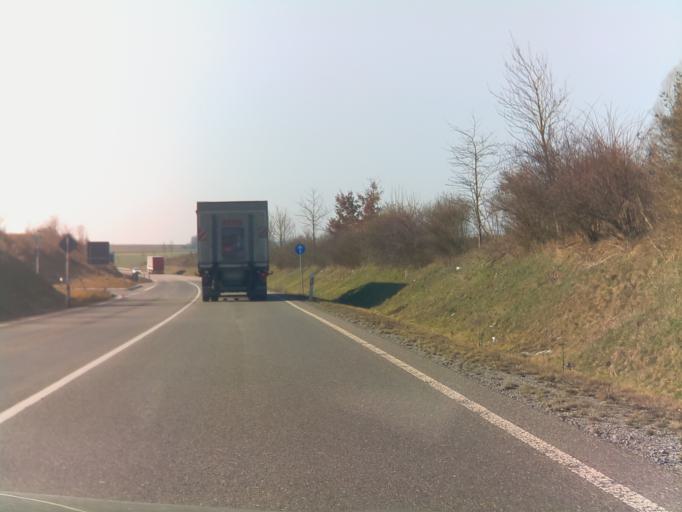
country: DE
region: Baden-Wuerttemberg
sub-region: Regierungsbezirk Stuttgart
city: Motzingen
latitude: 48.5009
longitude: 8.7925
